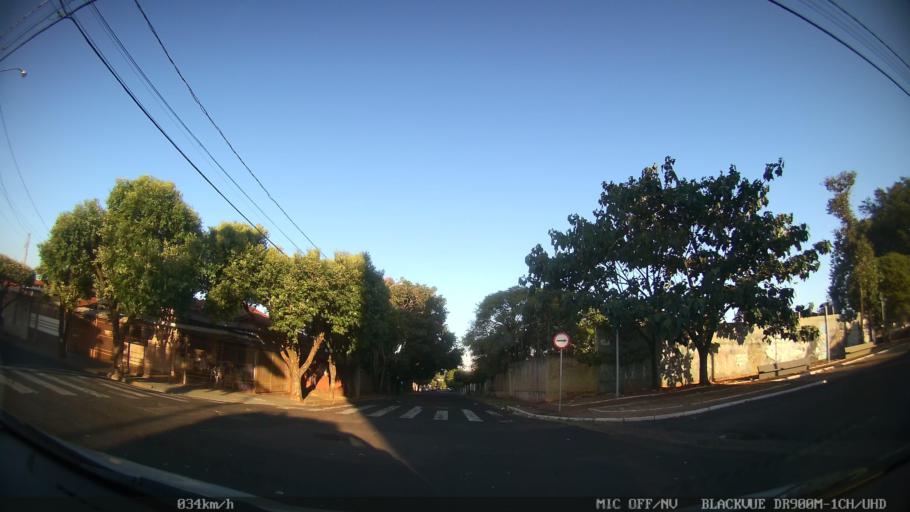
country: BR
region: Sao Paulo
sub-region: Sao Jose Do Rio Preto
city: Sao Jose do Rio Preto
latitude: -20.7979
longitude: -49.3840
